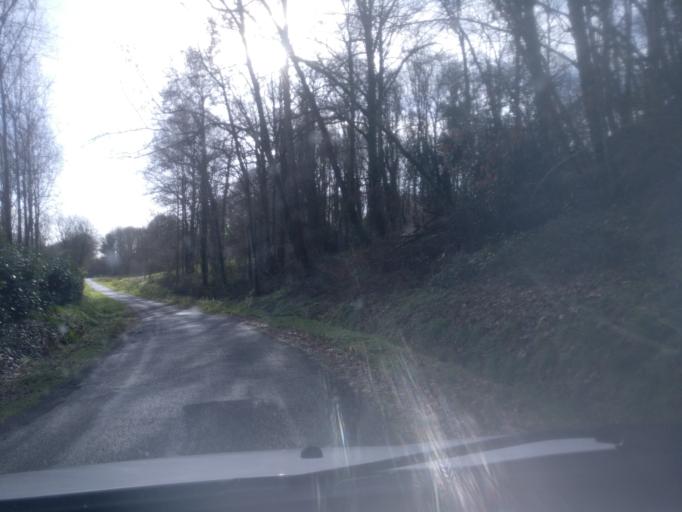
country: FR
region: Brittany
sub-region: Departement d'Ille-et-Vilaine
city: Antrain
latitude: 48.4943
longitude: -1.4965
